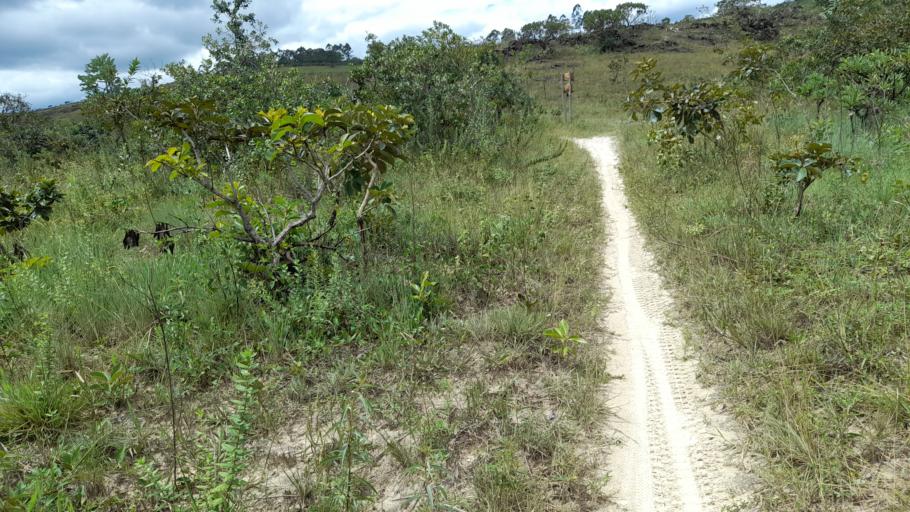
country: BR
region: Minas Gerais
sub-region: Sao Joao Del Rei
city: Sao Joao del Rei
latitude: -21.1242
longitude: -44.2777
